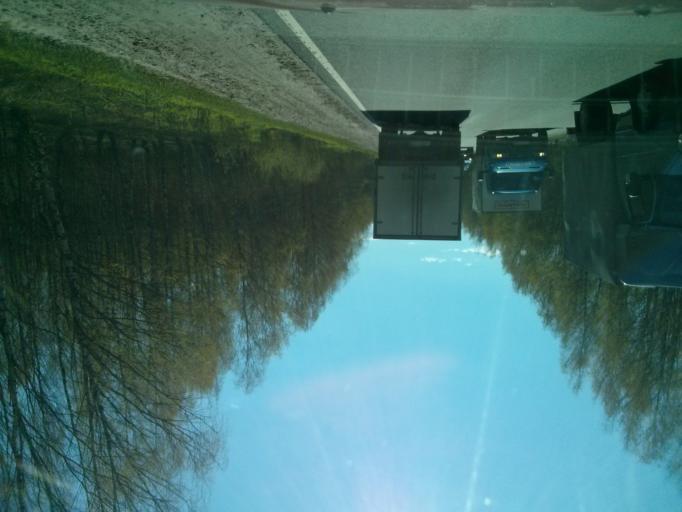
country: RU
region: Nizjnij Novgorod
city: Vorsma
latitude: 56.0172
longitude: 43.3476
